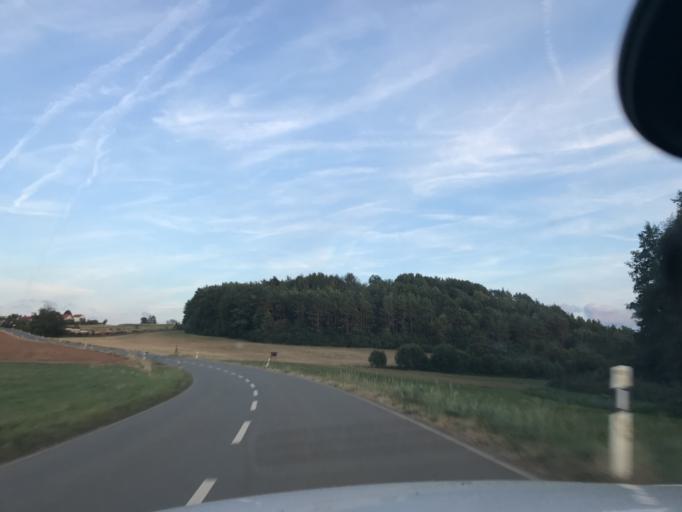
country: DE
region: Bavaria
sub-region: Upper Palatinate
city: Auerbach
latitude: 49.7349
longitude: 11.6035
